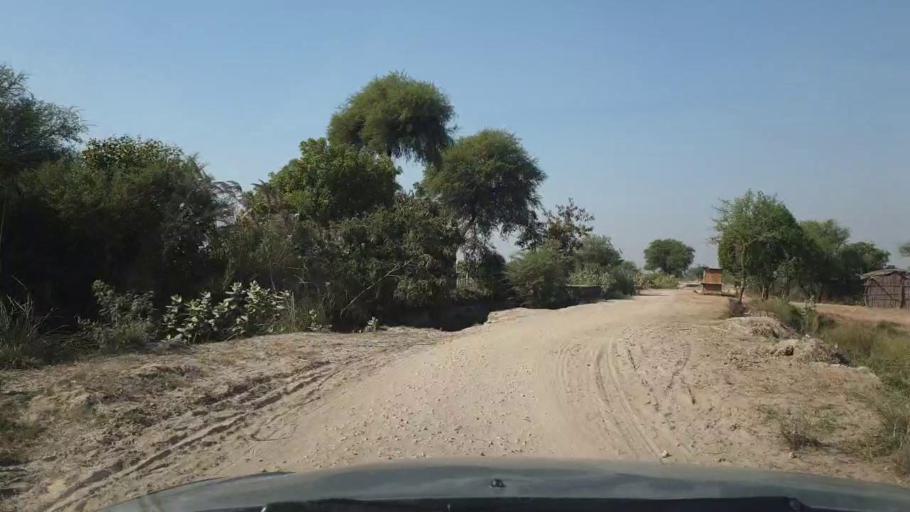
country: PK
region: Sindh
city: Tando Muhammad Khan
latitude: 24.9875
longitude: 68.5078
